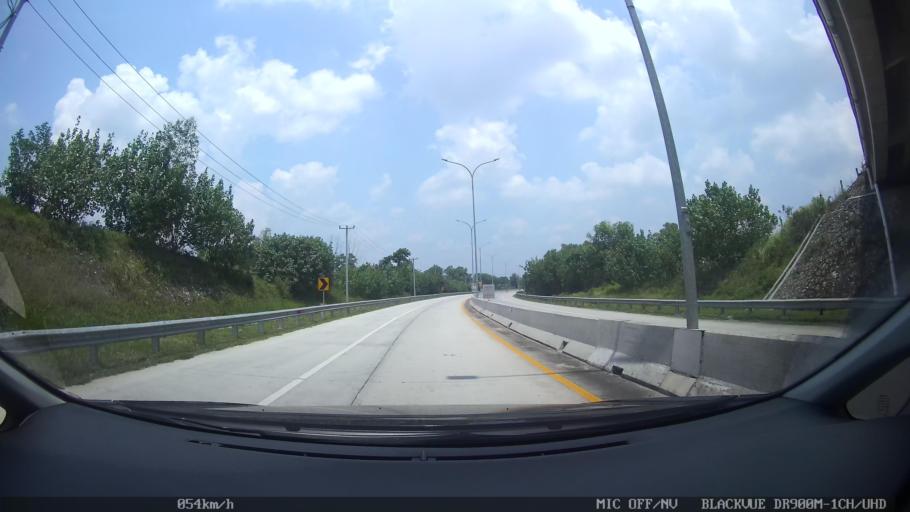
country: ID
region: Lampung
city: Natar
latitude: -5.2822
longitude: 105.2040
